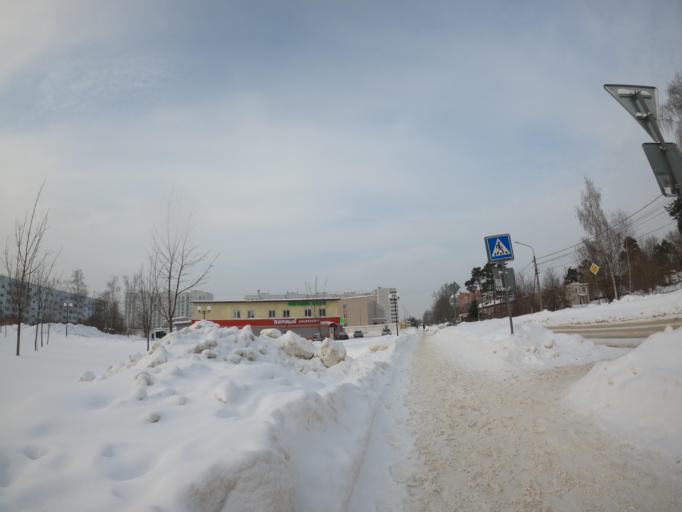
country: RU
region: Moskovskaya
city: Elektrogorsk
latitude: 55.8863
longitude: 38.7789
